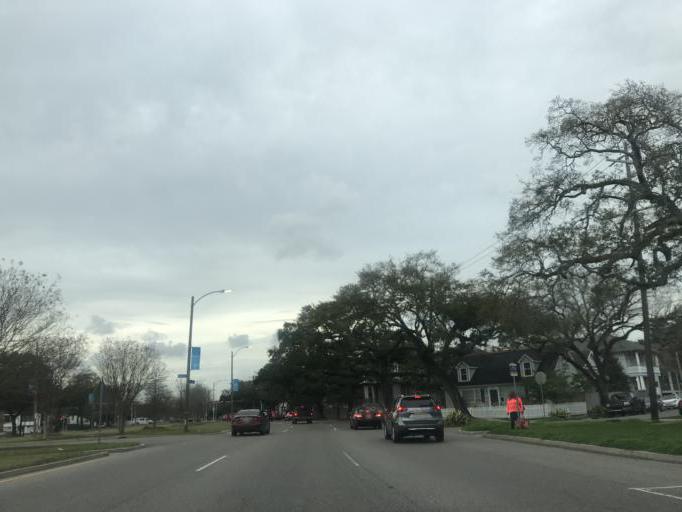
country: US
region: Louisiana
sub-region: Orleans Parish
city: New Orleans
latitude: 29.9406
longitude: -90.1080
